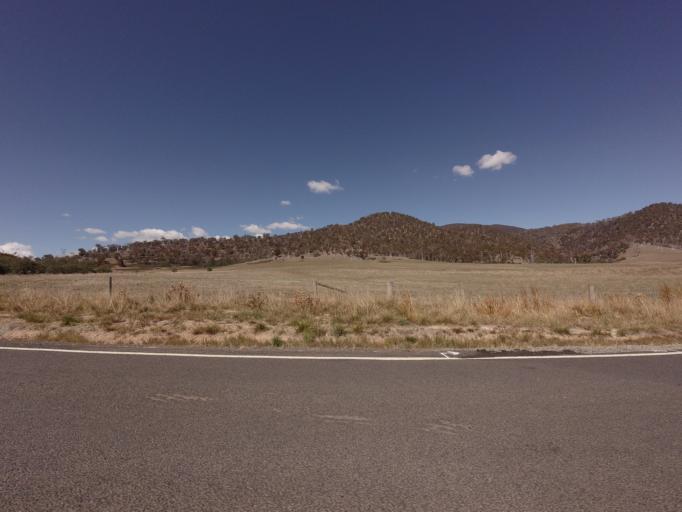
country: AU
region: Tasmania
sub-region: Break O'Day
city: St Helens
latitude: -41.6979
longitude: 147.8614
